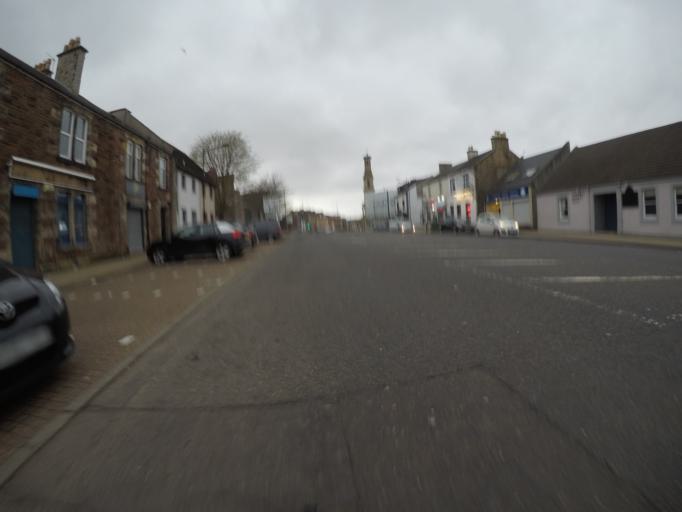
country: GB
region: Scotland
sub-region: North Ayrshire
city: Irvine
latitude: 55.6138
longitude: -4.6638
